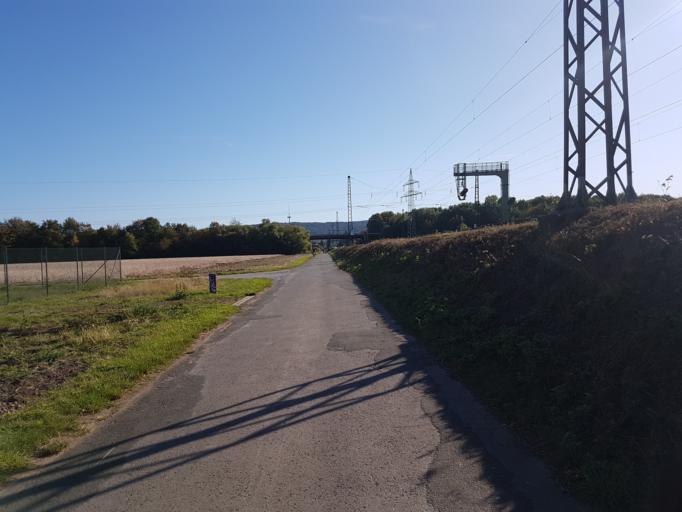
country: DE
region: North Rhine-Westphalia
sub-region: Regierungsbezirk Detmold
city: Minden
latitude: 52.2751
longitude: 8.9330
